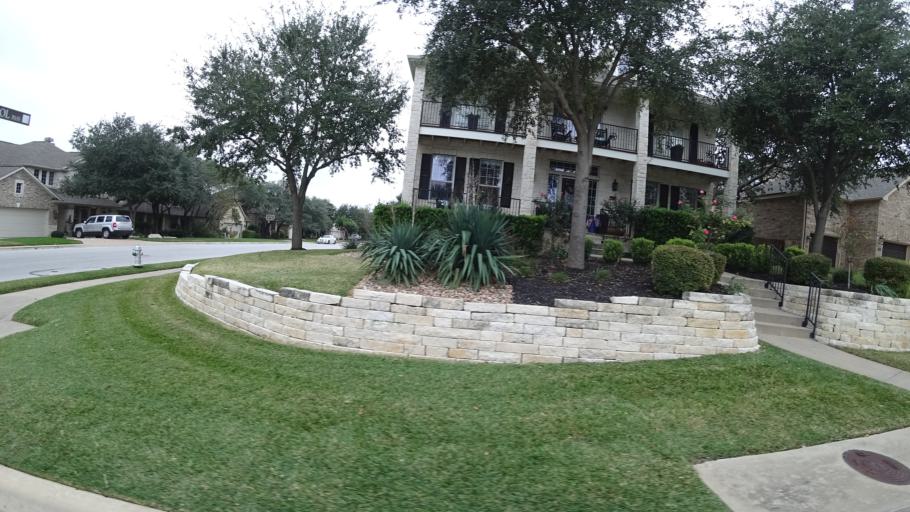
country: US
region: Texas
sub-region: Travis County
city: Hudson Bend
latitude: 30.3609
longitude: -97.8981
